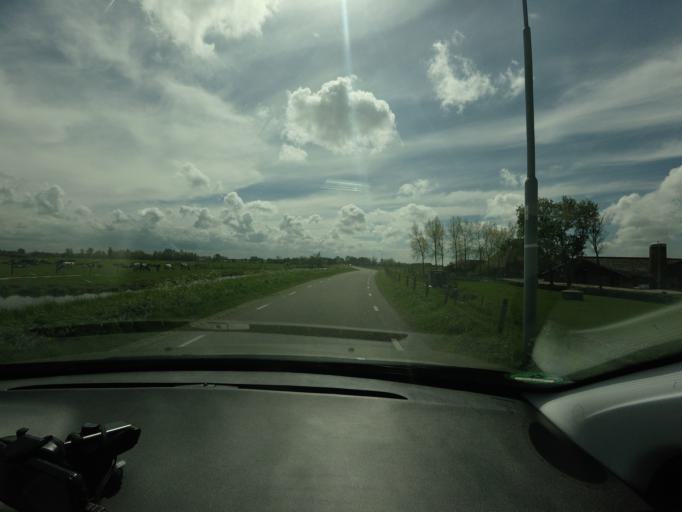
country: NL
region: North Holland
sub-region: Gemeente Beemster
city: Halfweg
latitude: 52.5684
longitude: 4.8342
